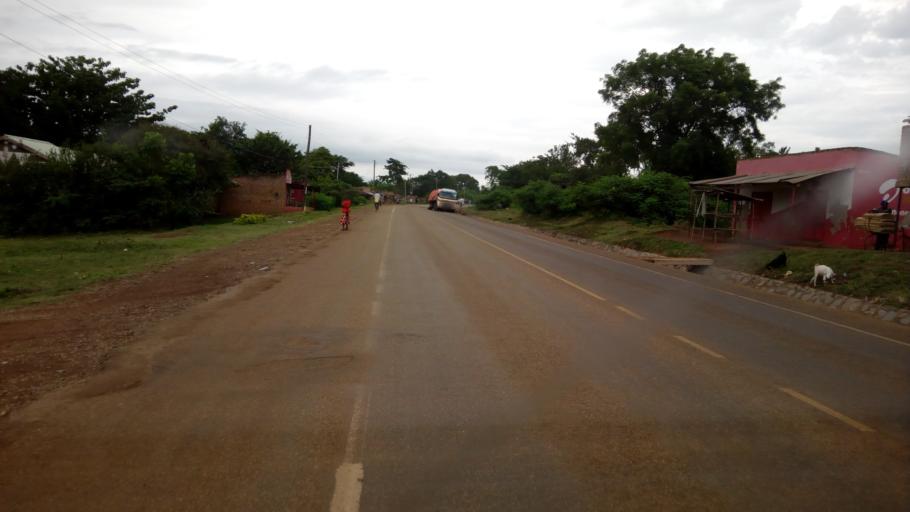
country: UG
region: Eastern Region
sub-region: Mbale District
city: Mbale
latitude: 0.9316
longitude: 34.1587
